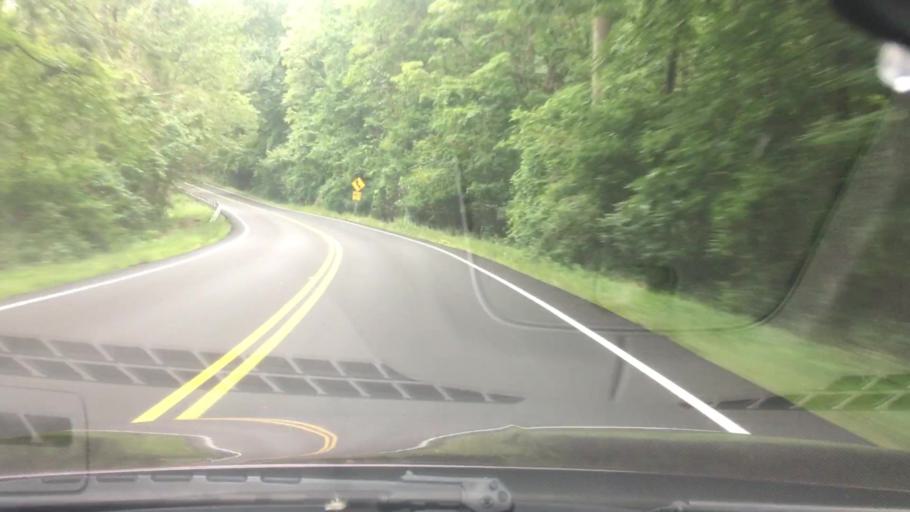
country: US
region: New York
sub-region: Dutchess County
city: Dover Plains
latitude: 41.8597
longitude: -73.5122
